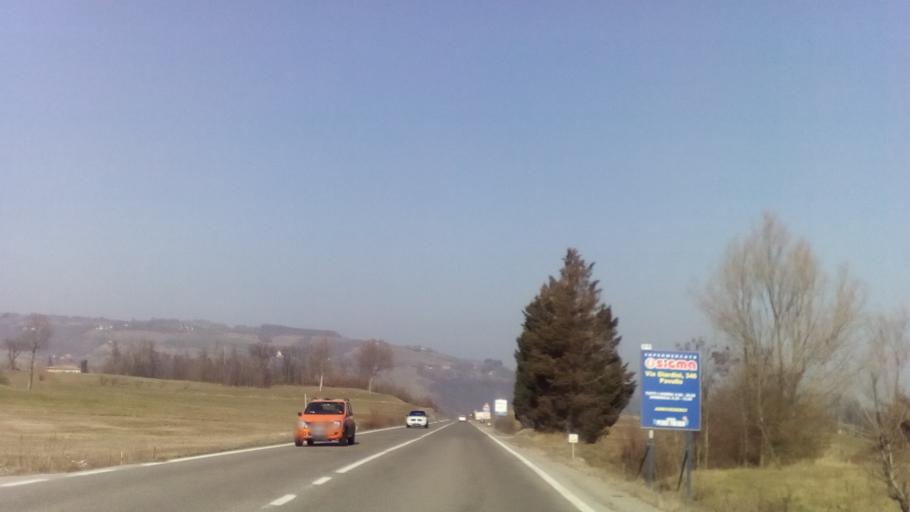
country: IT
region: Emilia-Romagna
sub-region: Provincia di Modena
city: Sant'Antonio
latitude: 44.3910
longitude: 10.8188
